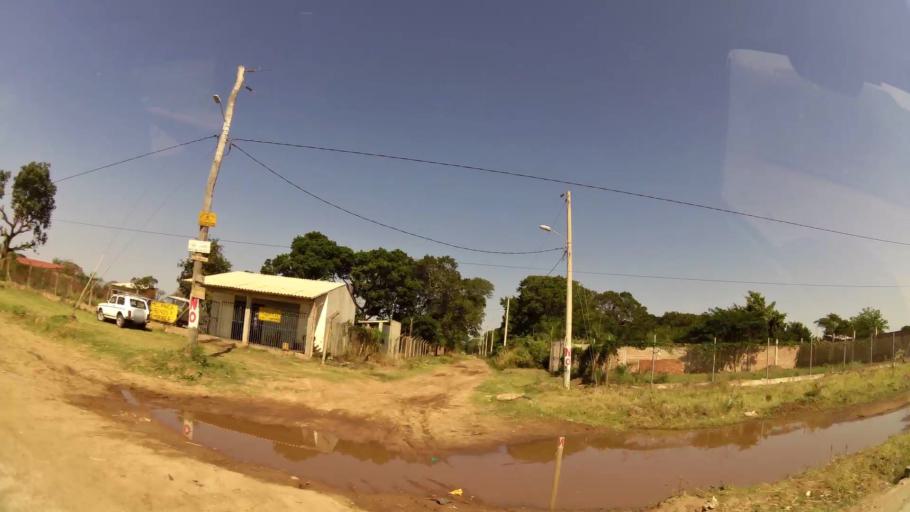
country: BO
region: Santa Cruz
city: Cotoca
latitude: -17.7234
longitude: -63.0806
